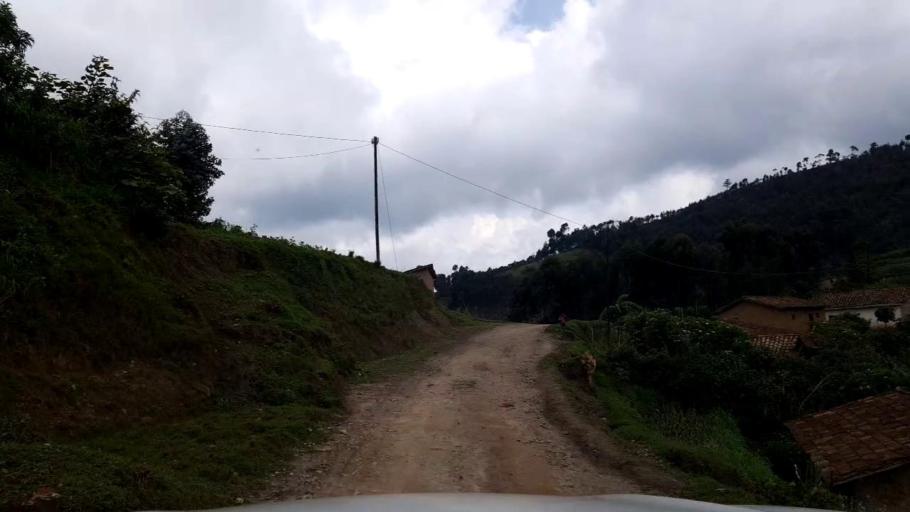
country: RW
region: Western Province
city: Kibuye
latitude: -1.9529
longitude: 29.4743
